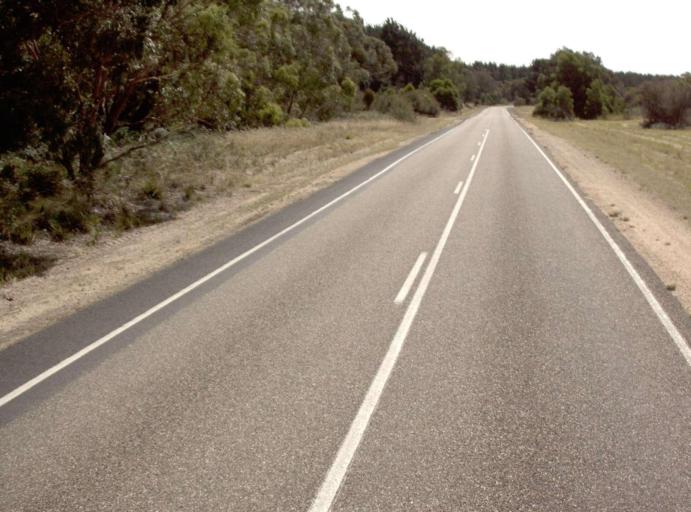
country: AU
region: Victoria
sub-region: Wellington
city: Sale
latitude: -38.1621
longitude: 146.9330
